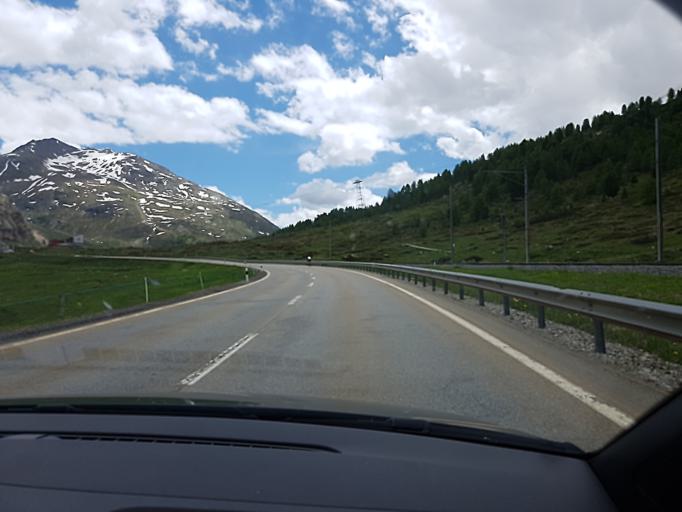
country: CH
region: Grisons
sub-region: Maloja District
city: Pontresina
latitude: 46.4438
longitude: 9.9734
